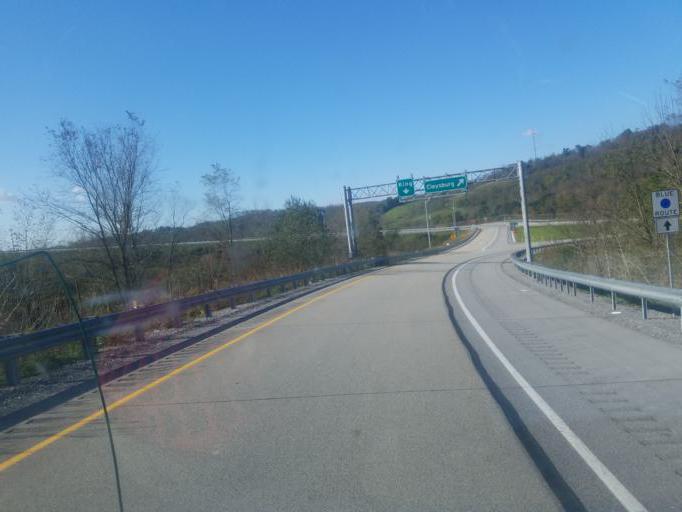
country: US
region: Pennsylvania
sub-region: Blair County
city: Claysburg
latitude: 40.2608
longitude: -78.4576
